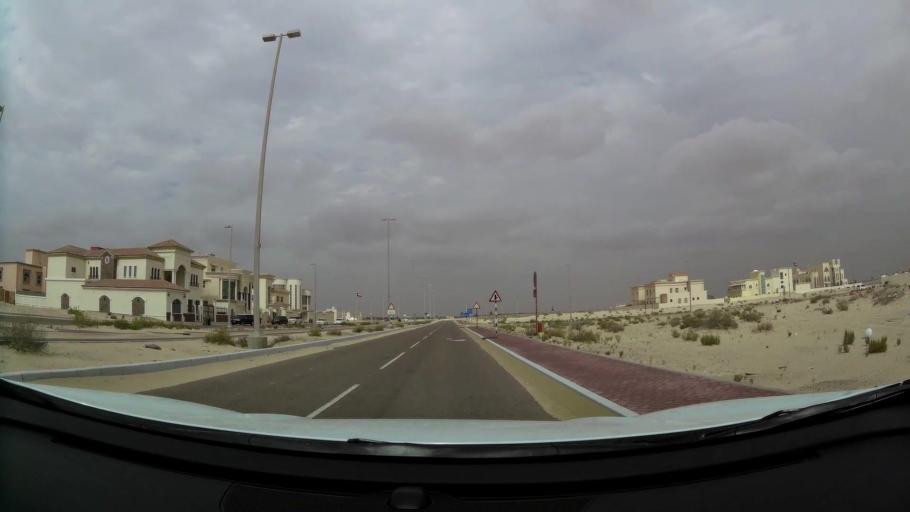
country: AE
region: Abu Dhabi
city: Abu Dhabi
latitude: 24.3979
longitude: 54.6555
